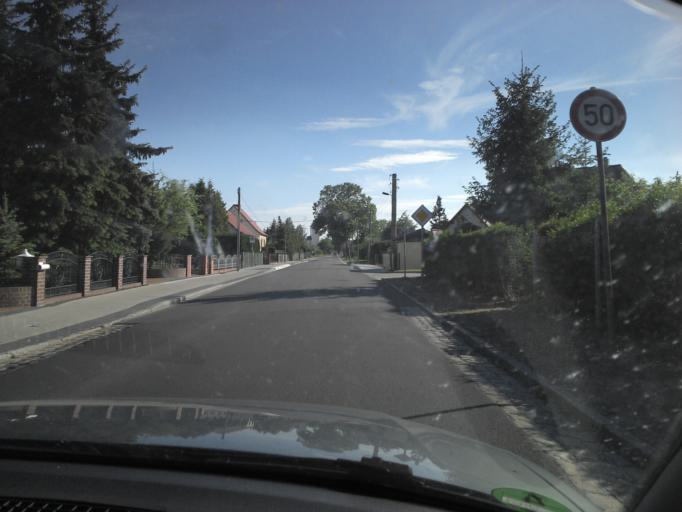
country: DE
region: Brandenburg
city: Vetschau
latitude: 51.7988
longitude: 14.0895
